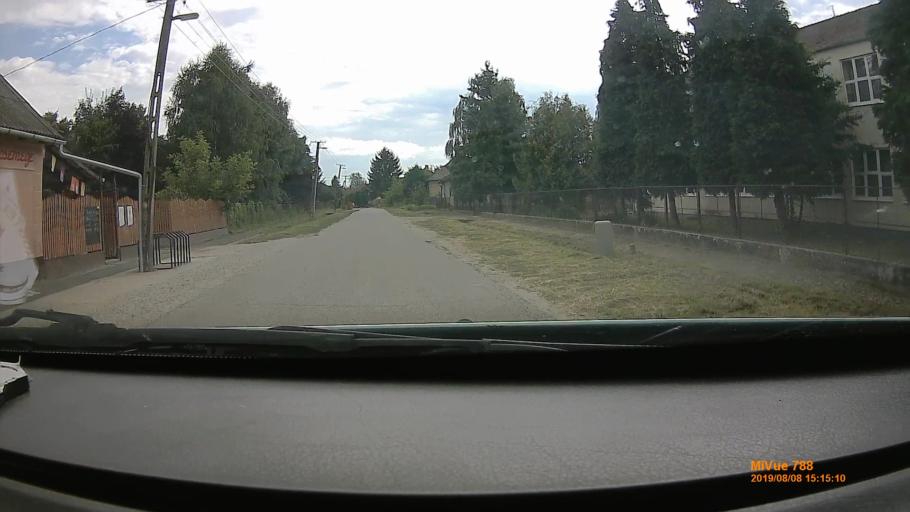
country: HU
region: Szabolcs-Szatmar-Bereg
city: Tunyogmatolcs
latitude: 47.9698
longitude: 22.4583
